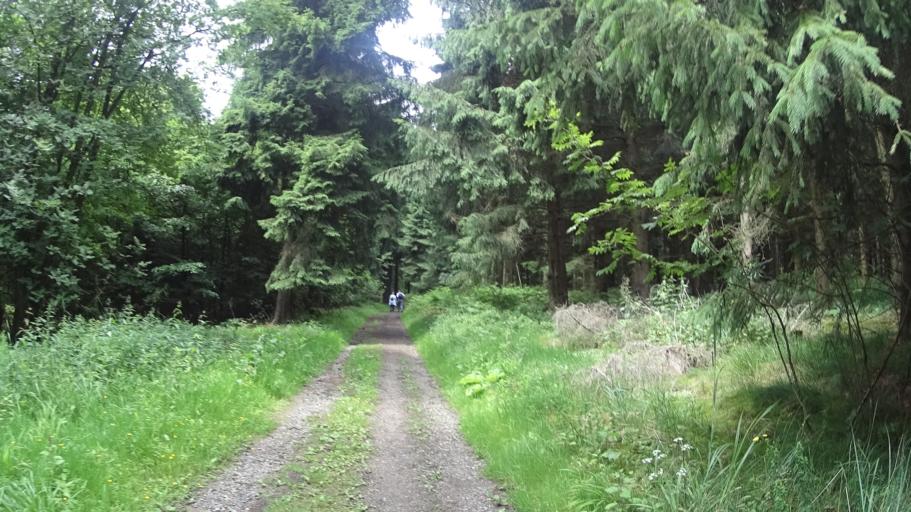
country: DE
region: Lower Saxony
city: Hameln
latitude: 52.1669
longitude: 9.3898
